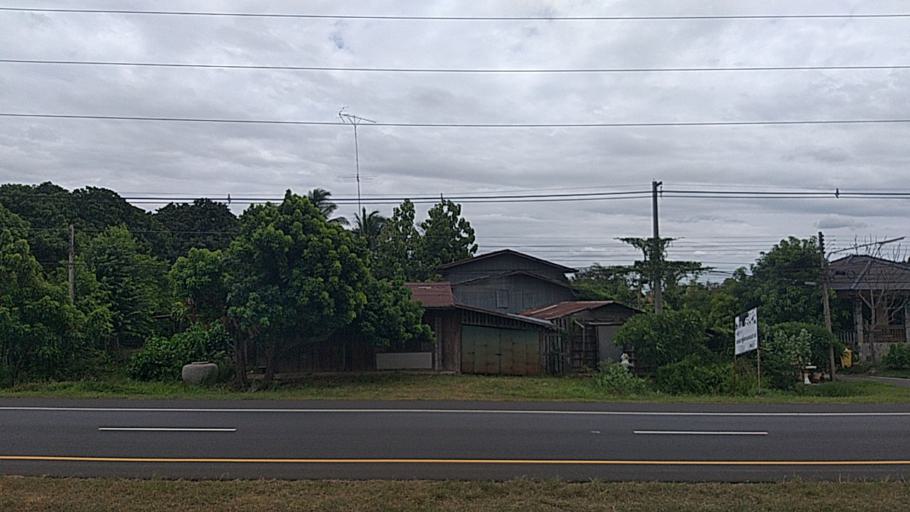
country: TH
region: Buriram
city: Chaloem Phra Kiat
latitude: 14.6088
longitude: 102.9220
